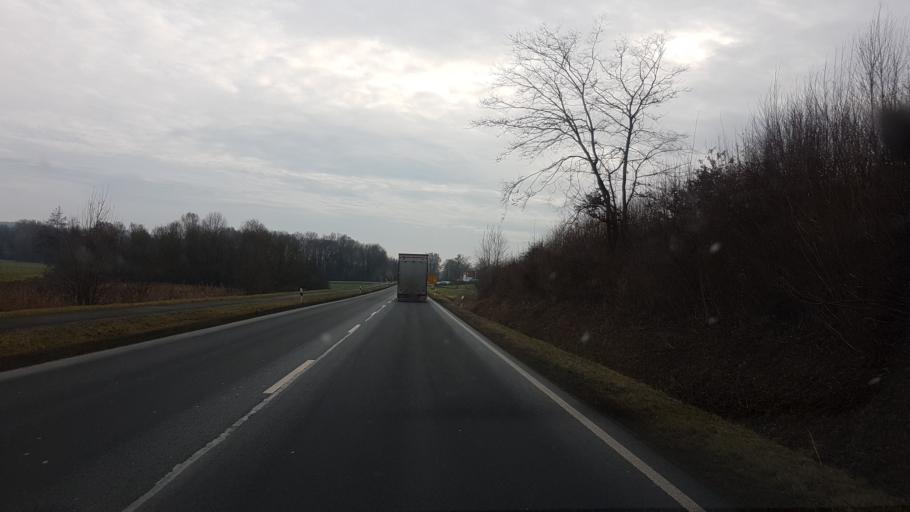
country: DE
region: Bavaria
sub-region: Regierungsbezirk Unterfranken
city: Rentweinsdorf
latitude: 50.0703
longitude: 10.7956
